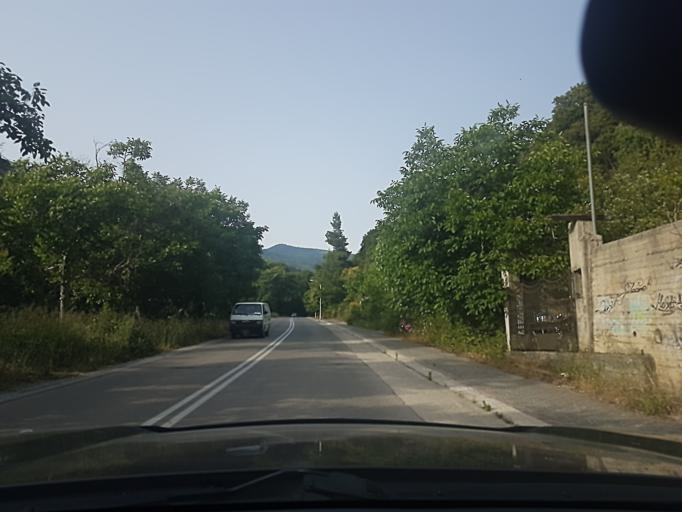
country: GR
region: Central Greece
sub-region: Nomos Evvoias
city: Yimnon
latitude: 38.5768
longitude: 23.8326
